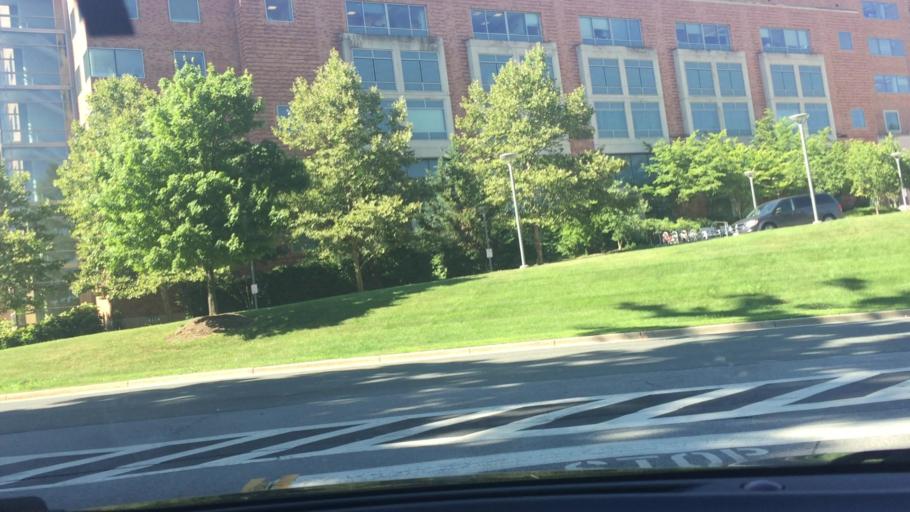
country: US
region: Maryland
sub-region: Montgomery County
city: Bethesda
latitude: 39.0037
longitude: -77.1035
